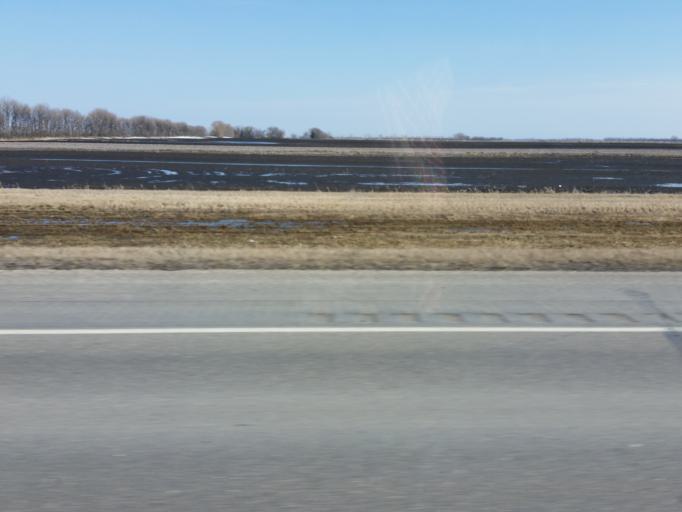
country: US
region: North Dakota
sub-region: Walsh County
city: Grafton
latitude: 48.2304
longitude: -97.3623
